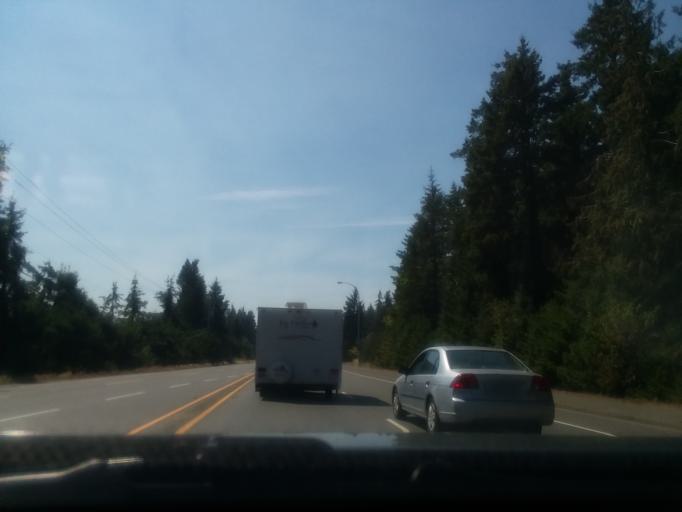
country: CA
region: British Columbia
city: Courtenay
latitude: 49.7097
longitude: -124.9671
